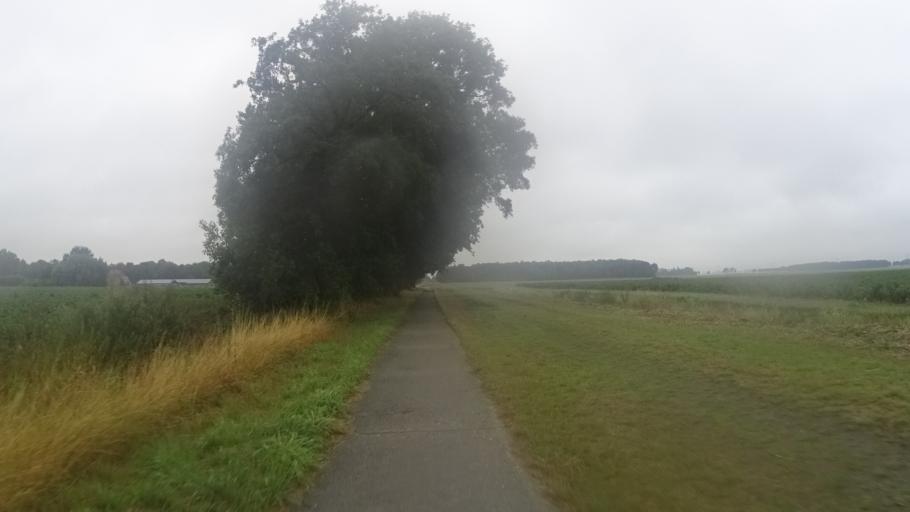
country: NL
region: Groningen
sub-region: Gemeente Veendam
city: Veendam
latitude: 53.1820
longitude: 6.8789
